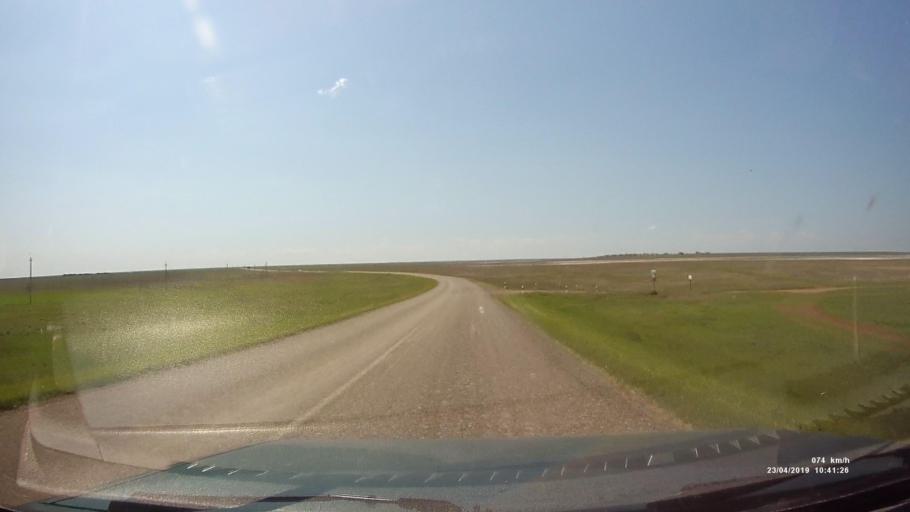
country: RU
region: Kalmykiya
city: Yashalta
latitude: 46.4940
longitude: 42.6379
